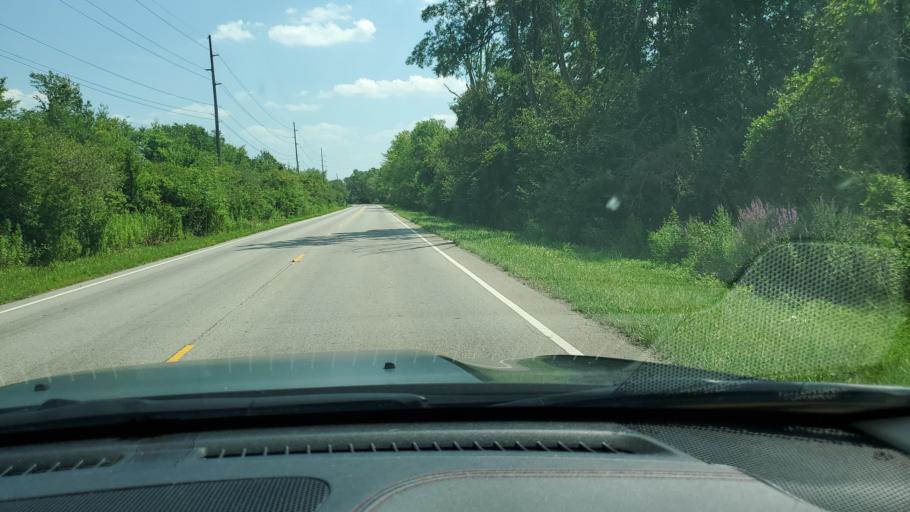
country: US
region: Ohio
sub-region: Trumbull County
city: Bolindale
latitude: 41.2122
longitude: -80.8040
